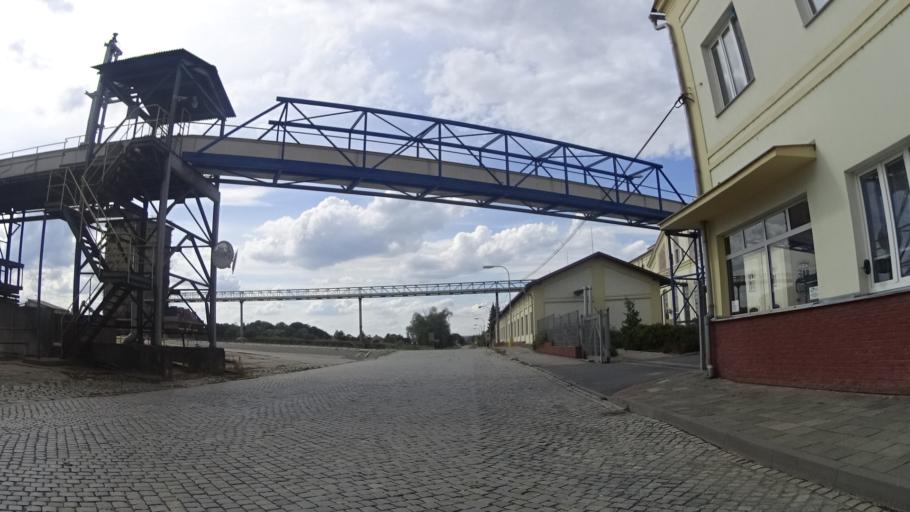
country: CZ
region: Olomoucky
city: Litovel
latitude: 49.7095
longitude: 17.0713
